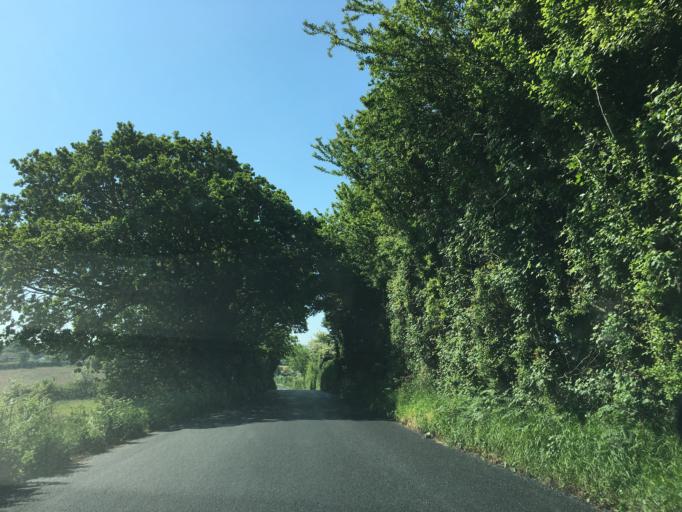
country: GB
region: England
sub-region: Isle of Wight
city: Newchurch
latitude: 50.6578
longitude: -1.2119
